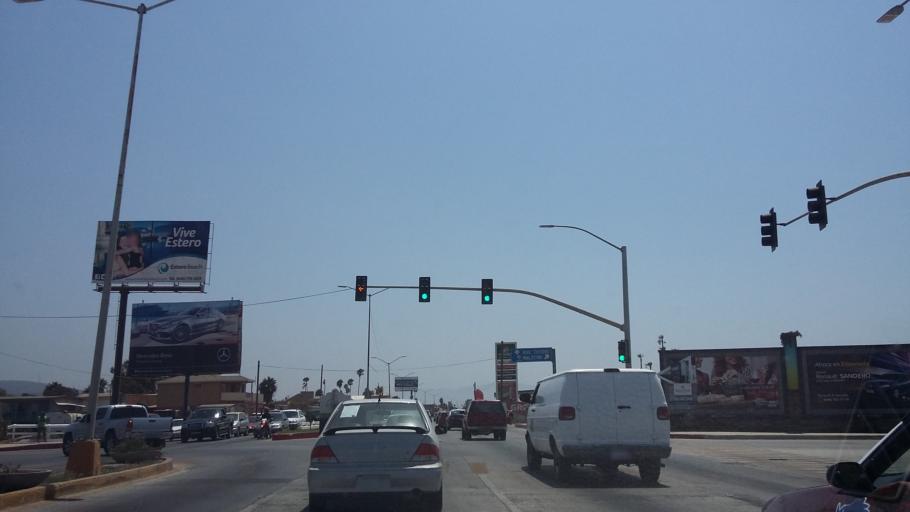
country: MX
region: Baja California
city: Ensenada
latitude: 31.8462
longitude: -116.6126
